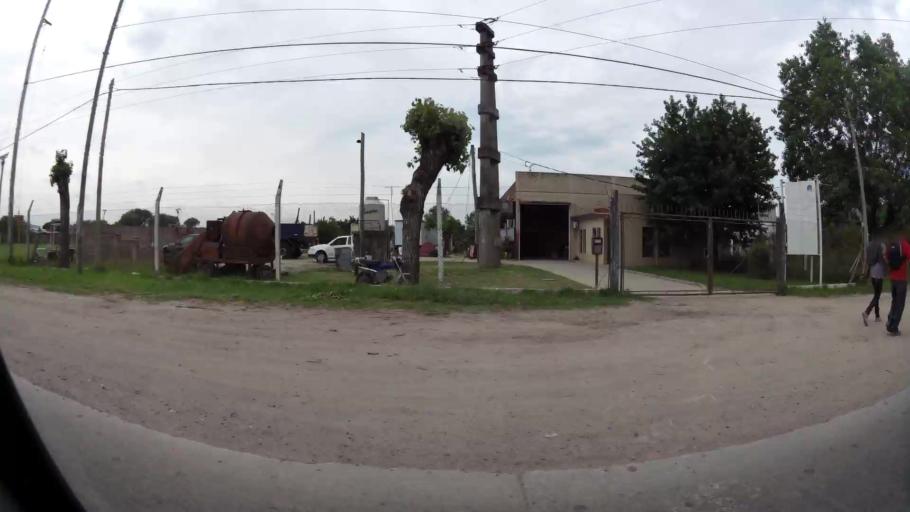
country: AR
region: Buenos Aires
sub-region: Partido de La Plata
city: La Plata
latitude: -34.9165
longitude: -58.0111
